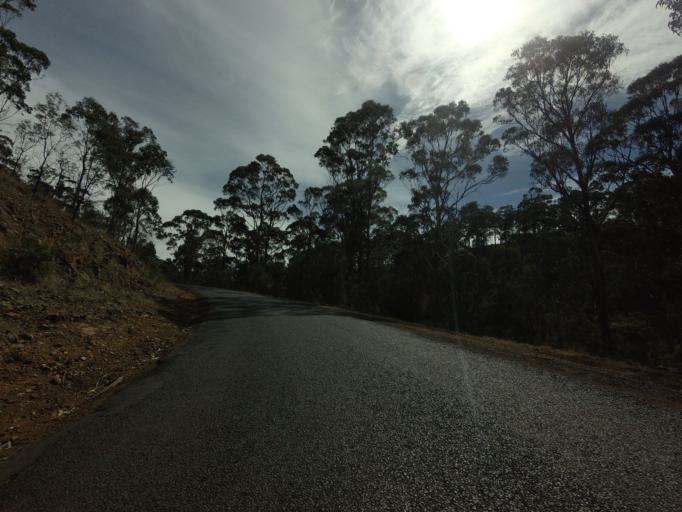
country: AU
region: Tasmania
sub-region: Sorell
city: Sorell
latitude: -42.5623
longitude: 147.6820
